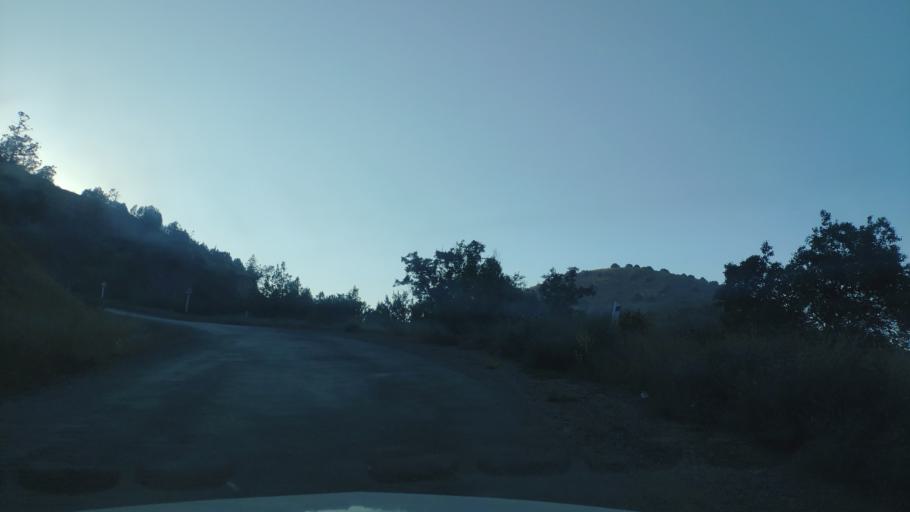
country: TJ
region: Viloyati Sughd
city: Ayni
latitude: 39.6397
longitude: 68.4735
